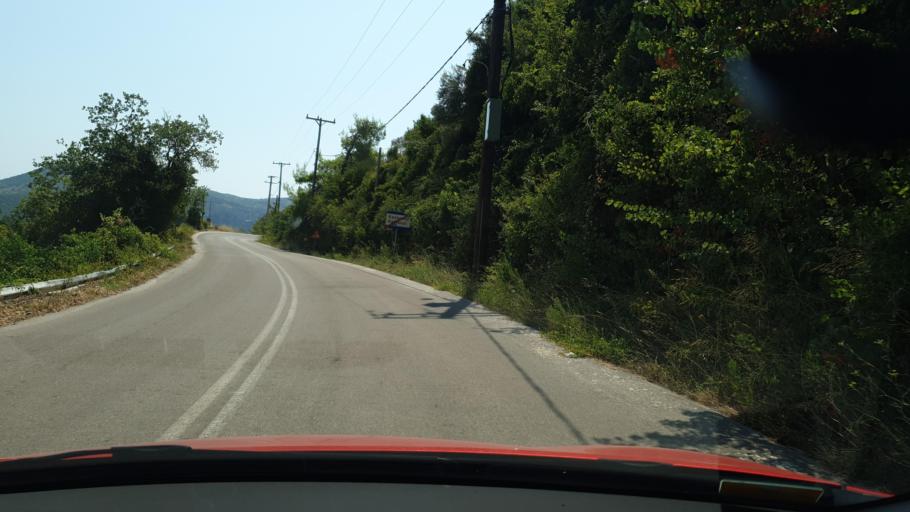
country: GR
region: Central Greece
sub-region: Nomos Evvoias
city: Kymi
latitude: 38.6130
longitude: 24.0788
